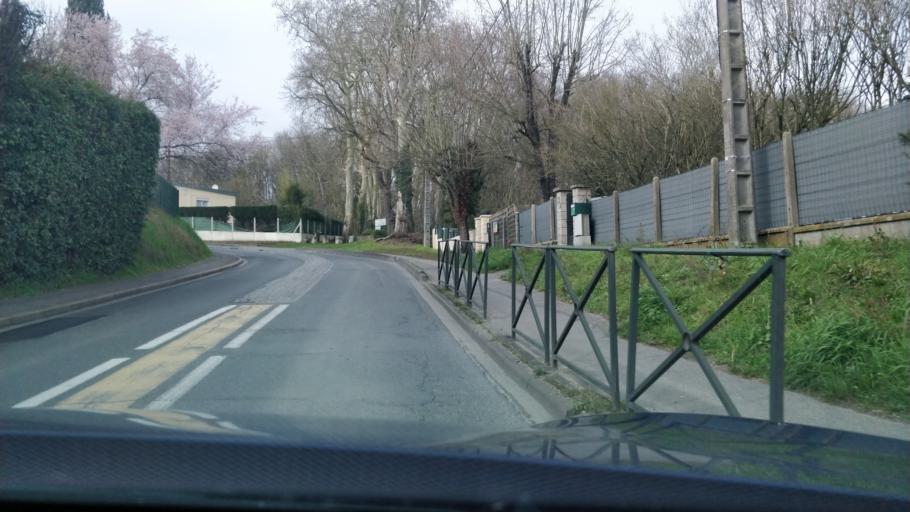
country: FR
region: Ile-de-France
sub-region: Departement de l'Essonne
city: Arpajon
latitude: 48.5966
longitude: 2.2540
